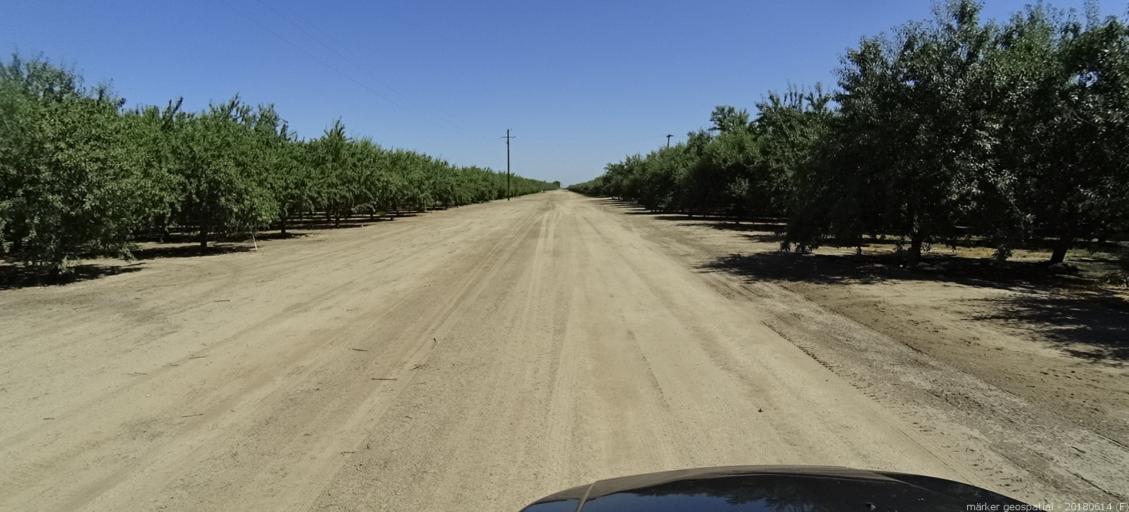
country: US
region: California
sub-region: Madera County
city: Fairmead
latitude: 36.9300
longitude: -120.2242
